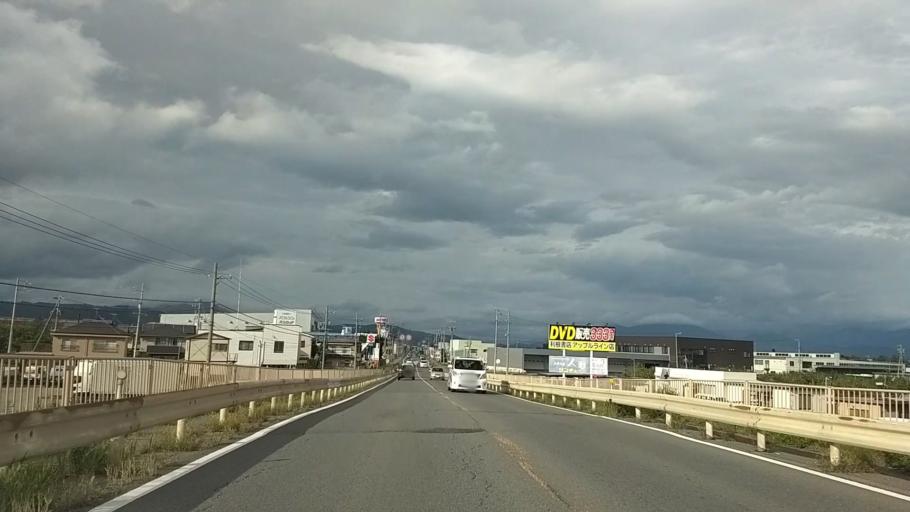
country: JP
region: Nagano
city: Suzaka
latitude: 36.6654
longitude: 138.2628
